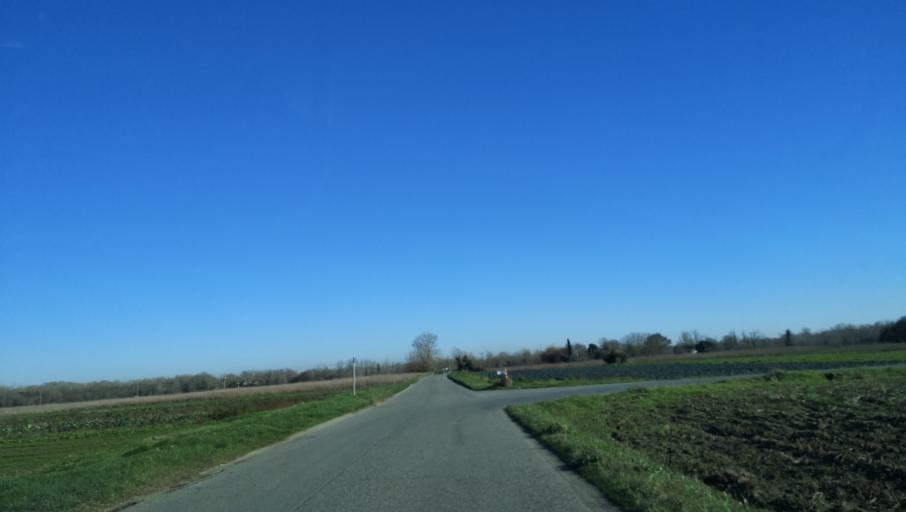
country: FR
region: Midi-Pyrenees
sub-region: Departement de la Haute-Garonne
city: Beauzelle
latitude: 43.6550
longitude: 1.3926
